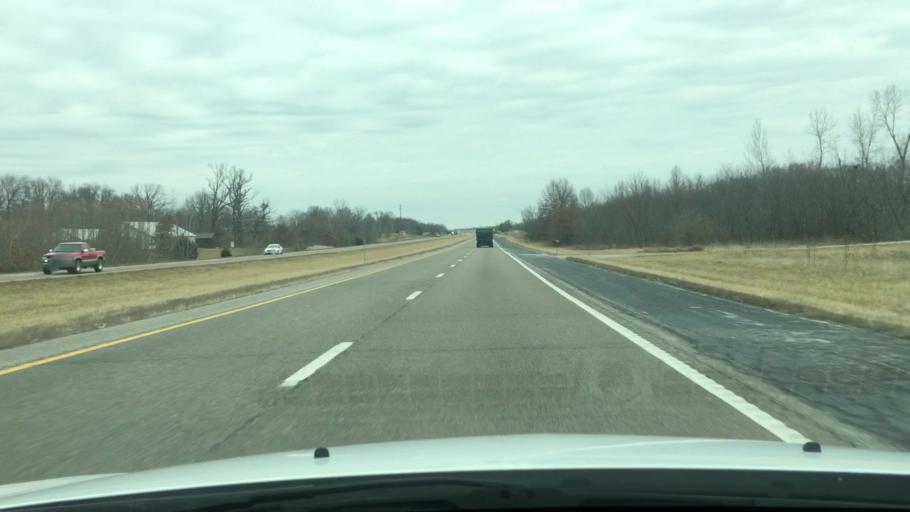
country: US
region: Missouri
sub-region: Audrain County
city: Mexico
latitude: 39.0460
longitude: -91.8935
